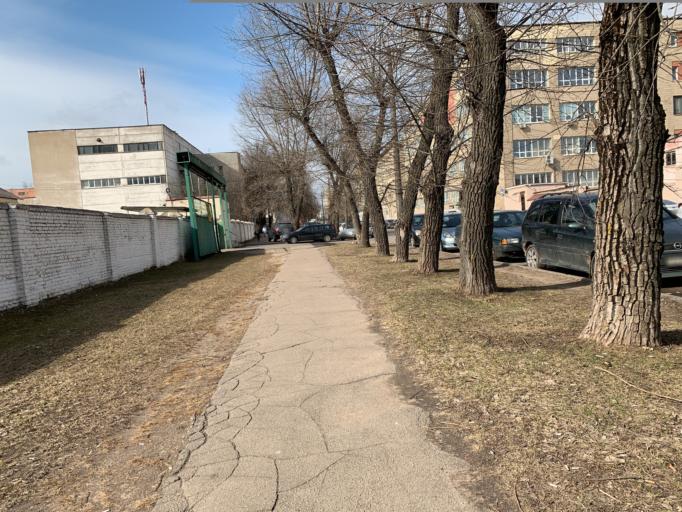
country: BY
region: Minsk
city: Minsk
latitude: 53.9107
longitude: 27.6037
